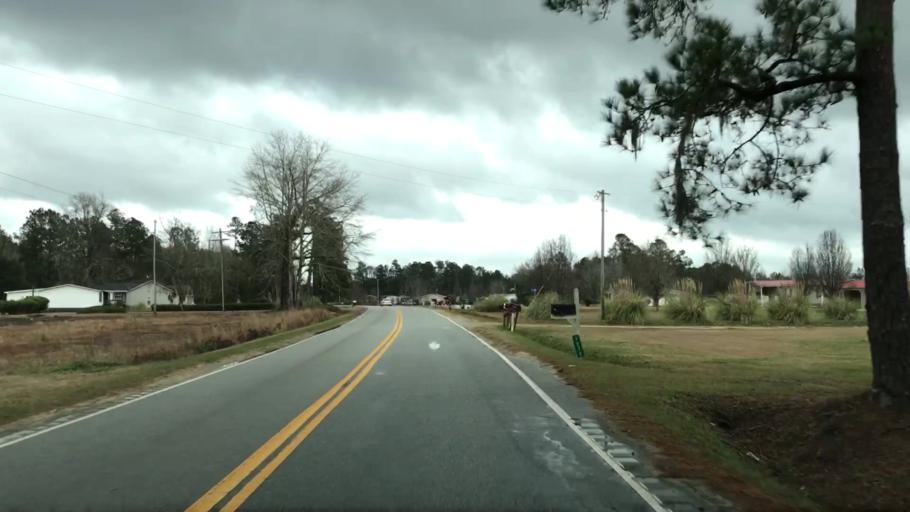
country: US
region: South Carolina
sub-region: Williamsburg County
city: Andrews
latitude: 33.4937
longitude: -79.5068
